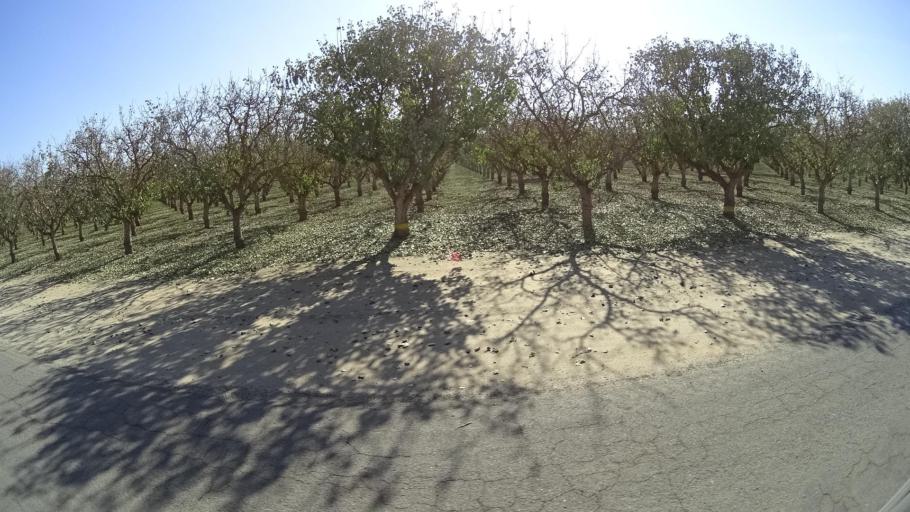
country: US
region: California
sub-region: Kern County
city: McFarland
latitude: 35.6456
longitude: -119.1839
